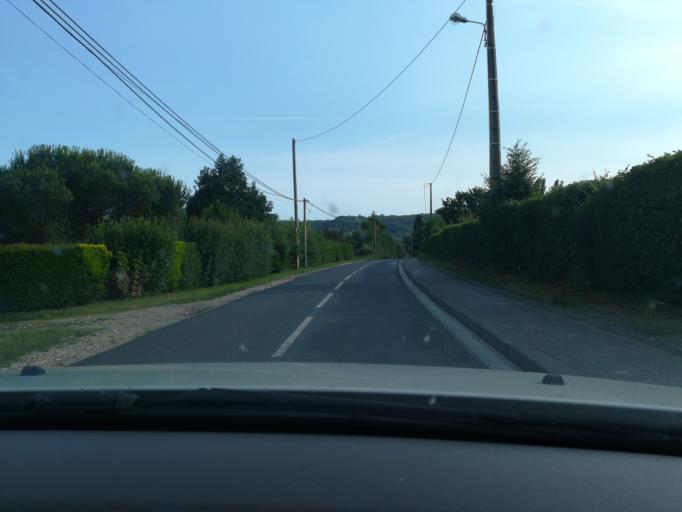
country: FR
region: Haute-Normandie
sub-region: Departement de la Seine-Maritime
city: Sahurs
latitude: 49.3617
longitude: 0.9476
